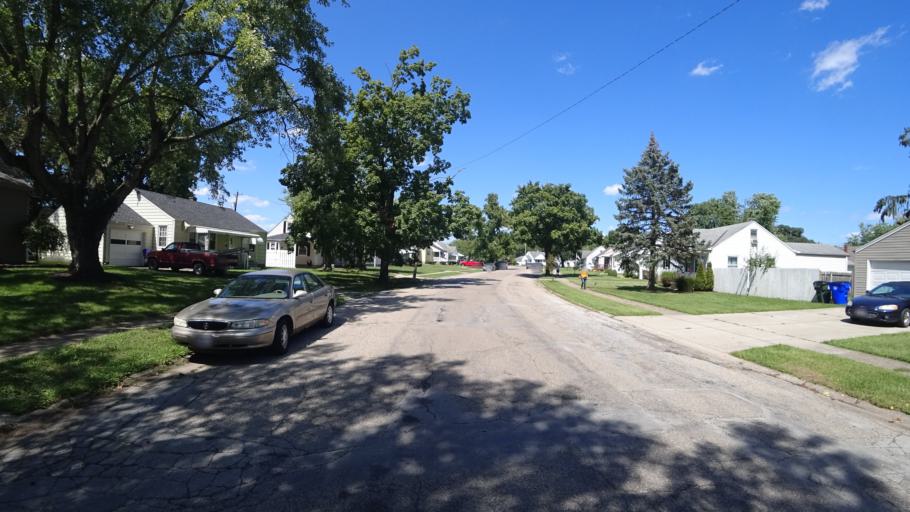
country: US
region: Ohio
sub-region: Butler County
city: Hamilton
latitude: 39.4047
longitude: -84.5329
